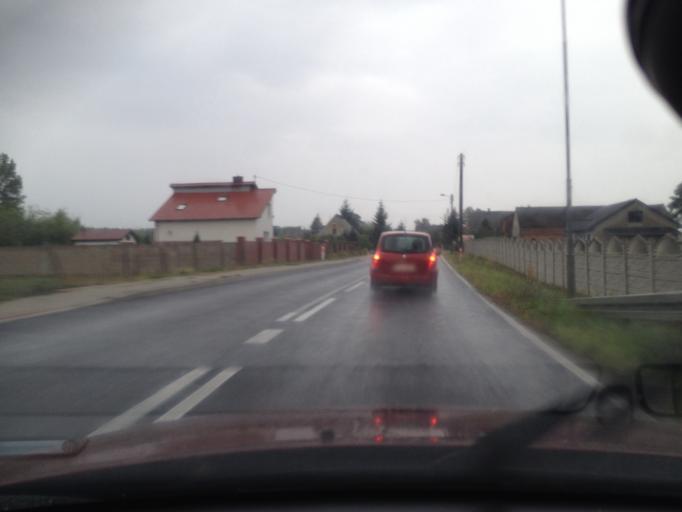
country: PL
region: Lubusz
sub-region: Powiat zaganski
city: Zagan
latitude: 51.6655
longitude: 15.3126
